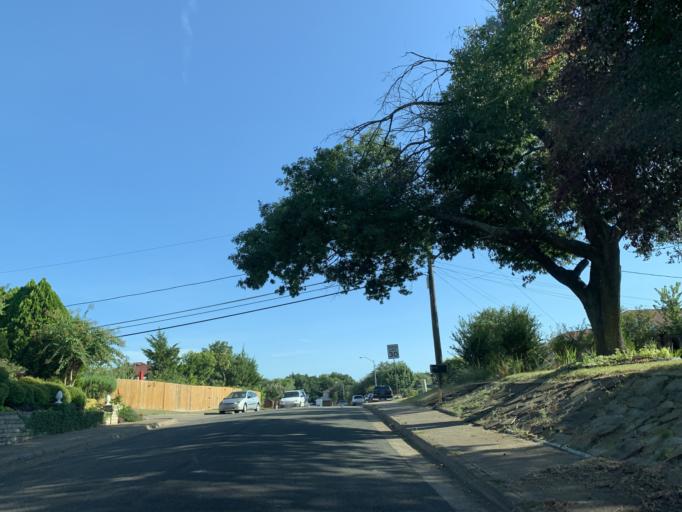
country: US
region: Texas
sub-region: Dallas County
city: Cockrell Hill
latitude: 32.7094
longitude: -96.8865
